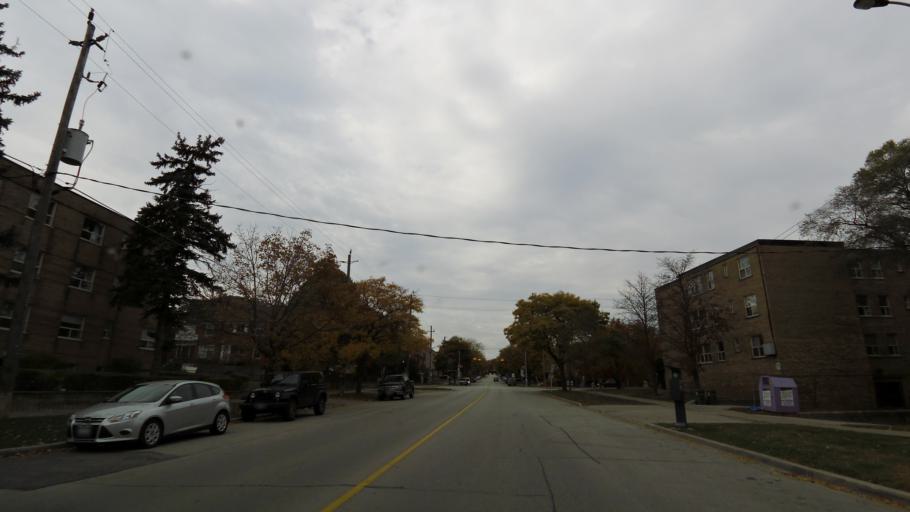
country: CA
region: Ontario
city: Etobicoke
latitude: 43.6636
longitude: -79.5208
